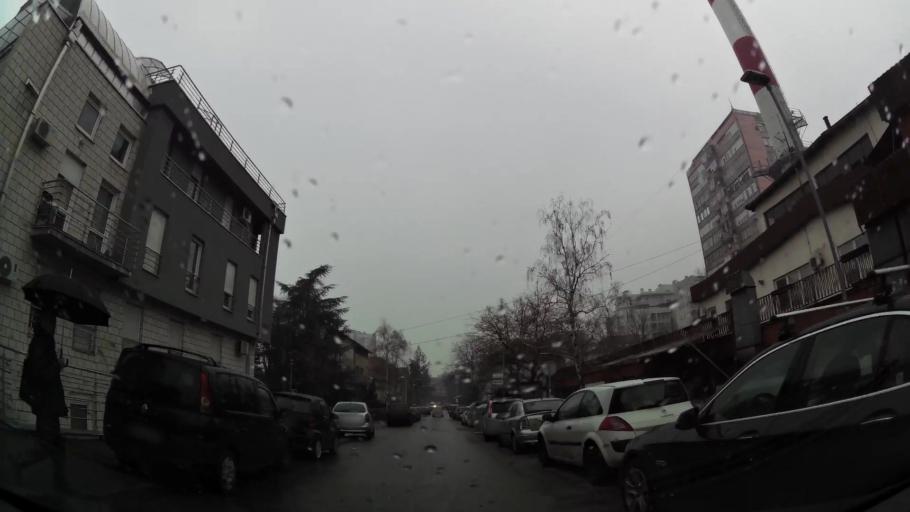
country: RS
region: Central Serbia
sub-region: Belgrade
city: Cukarica
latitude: 44.7794
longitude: 20.4147
